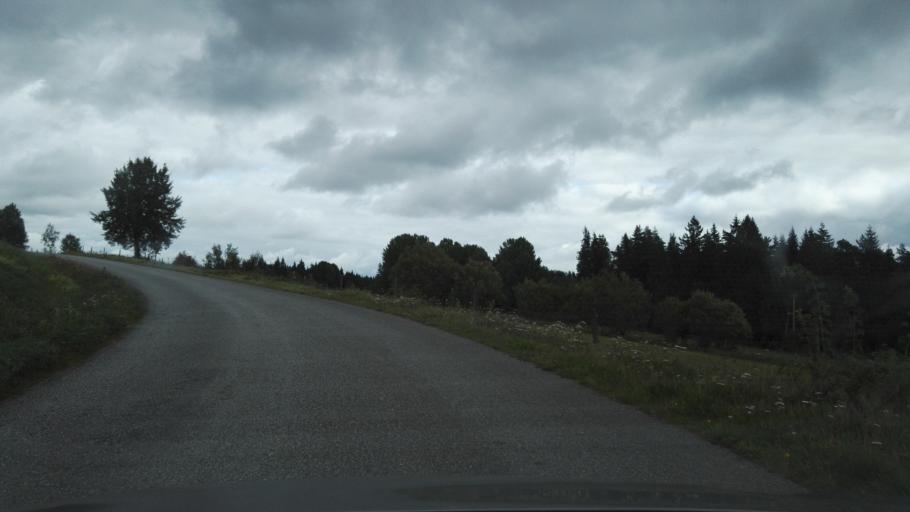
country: SE
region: Joenkoeping
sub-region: Vetlanda Kommun
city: Landsbro
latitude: 57.2891
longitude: 14.8341
